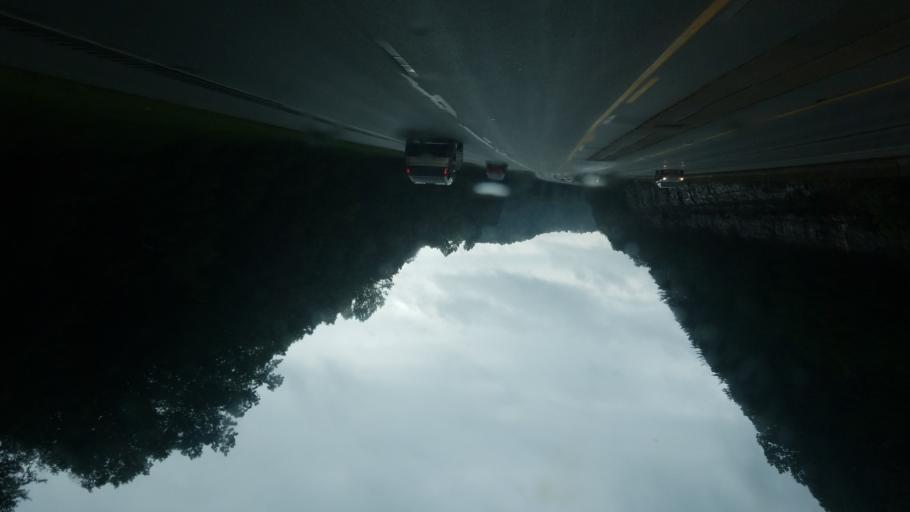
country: US
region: Kentucky
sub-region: Rowan County
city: Morehead
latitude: 38.1804
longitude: -83.4662
